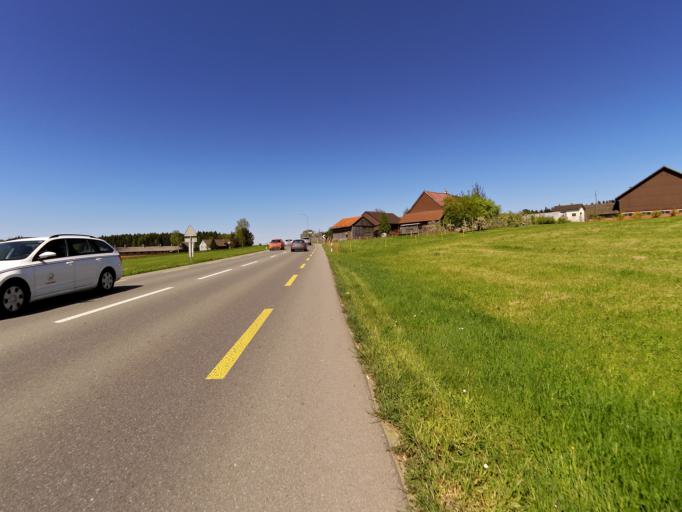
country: CH
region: Thurgau
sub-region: Weinfelden District
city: Berg
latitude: 47.5871
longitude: 9.1702
